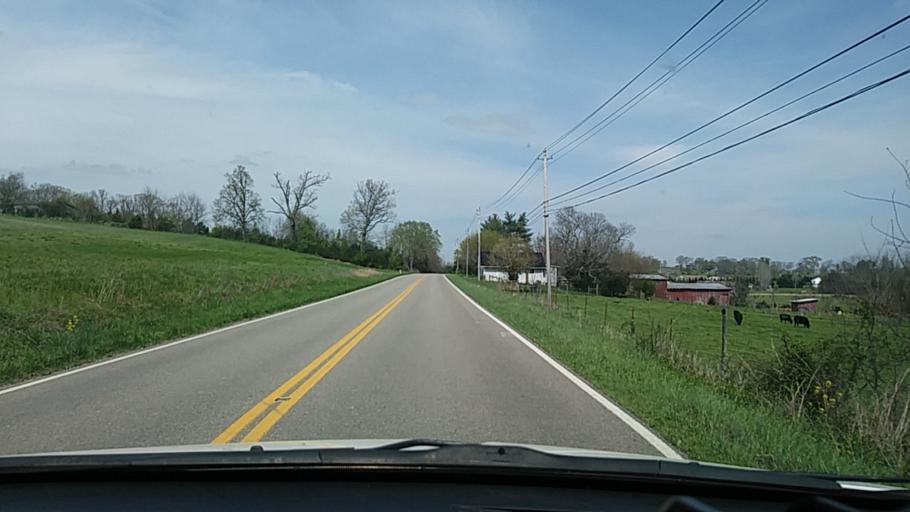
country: US
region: Tennessee
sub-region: Greene County
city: Greeneville
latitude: 36.1003
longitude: -82.7850
